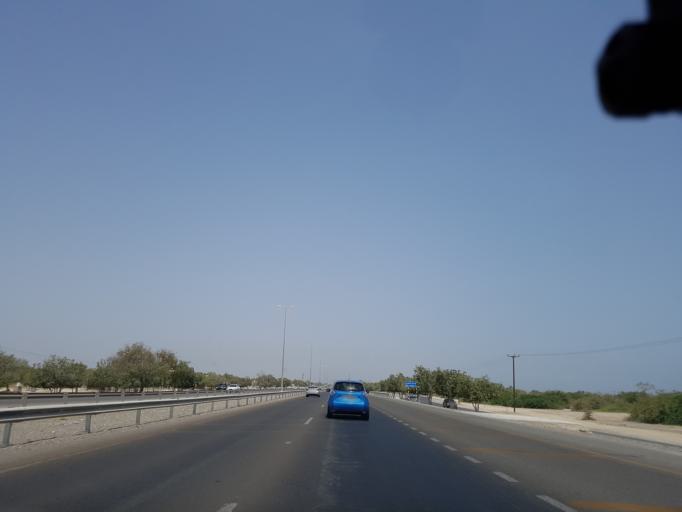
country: OM
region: Al Batinah
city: Saham
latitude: 24.2140
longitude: 56.8441
